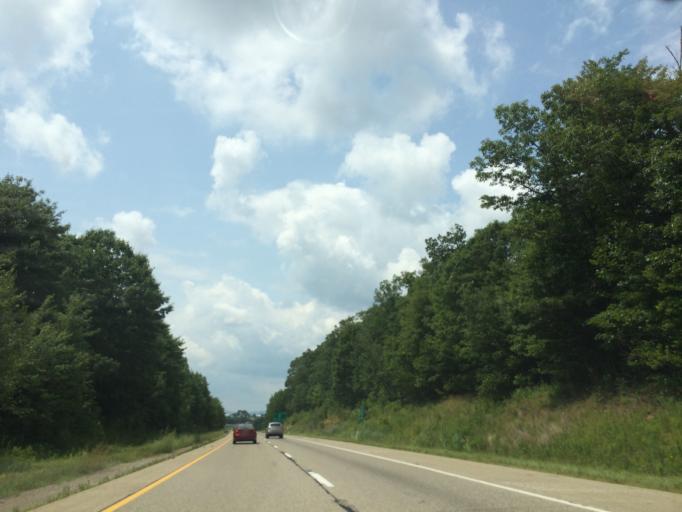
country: US
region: Pennsylvania
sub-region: Luzerne County
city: Conyngham
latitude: 41.0315
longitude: -76.0681
